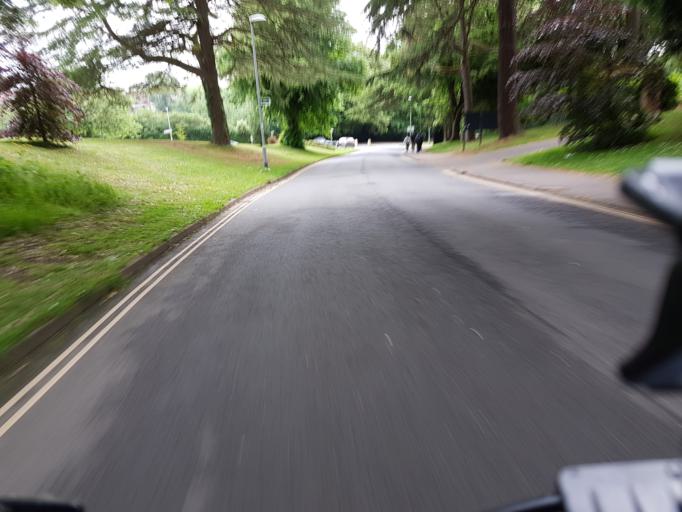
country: GB
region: England
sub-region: Devon
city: Exeter
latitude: 50.7328
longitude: -3.5376
